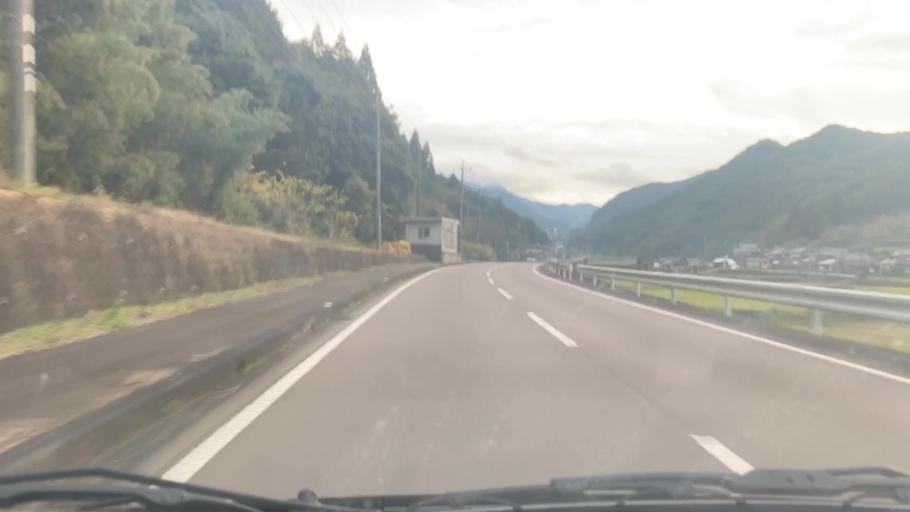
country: JP
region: Saga Prefecture
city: Kashima
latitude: 33.0676
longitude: 130.0703
